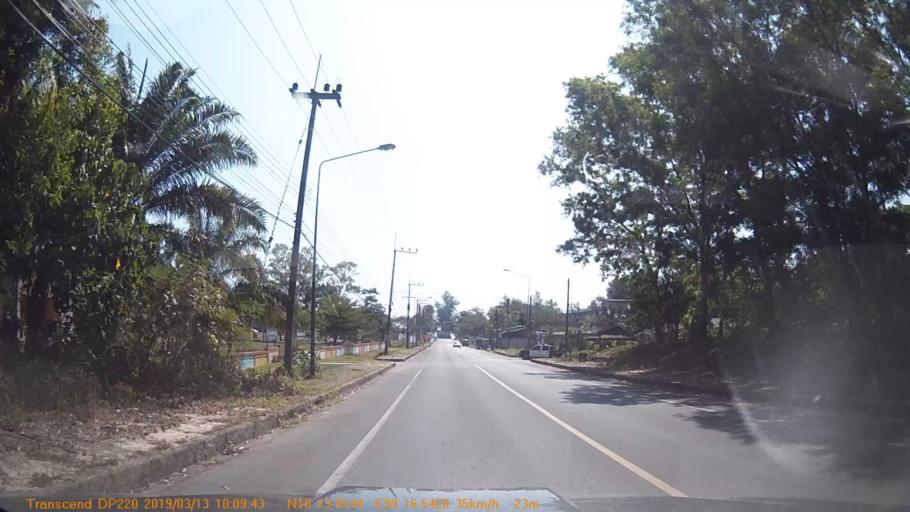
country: TH
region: Chumphon
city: Chumphon
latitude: 10.3985
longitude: 99.2759
